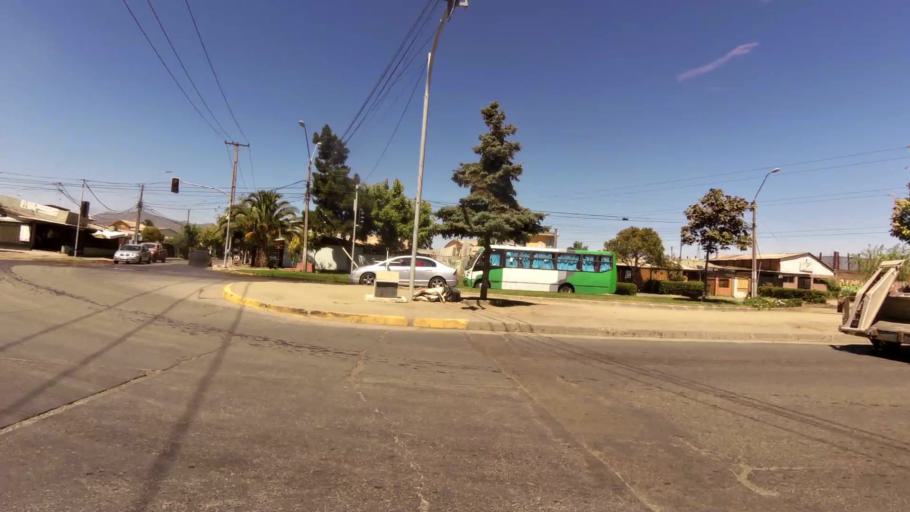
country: CL
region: O'Higgins
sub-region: Provincia de Cachapoal
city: Rancagua
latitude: -34.1559
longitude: -70.7250
